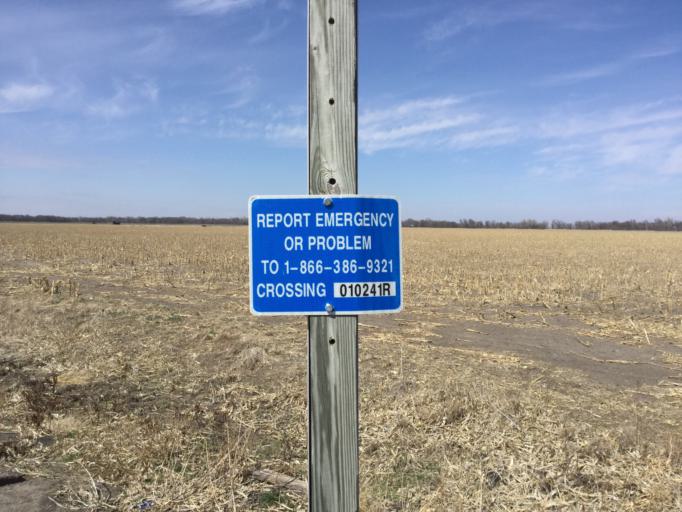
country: US
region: Kansas
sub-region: Barton County
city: Hoisington
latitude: 38.4343
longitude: -98.9188
